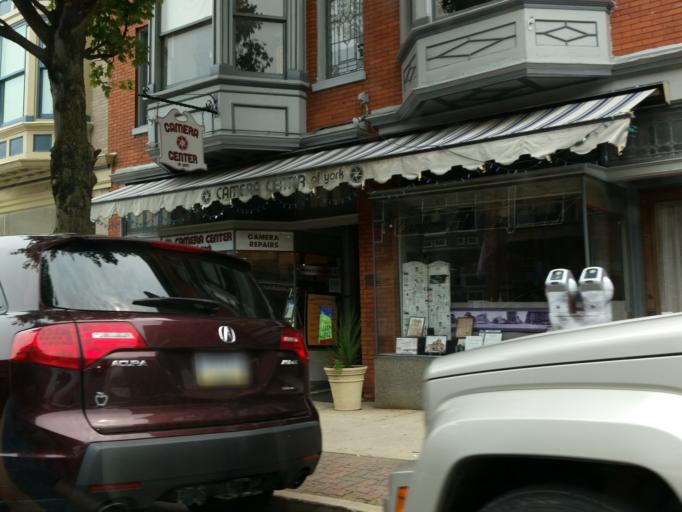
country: US
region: Pennsylvania
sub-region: York County
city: York
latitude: 39.9624
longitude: -76.7299
